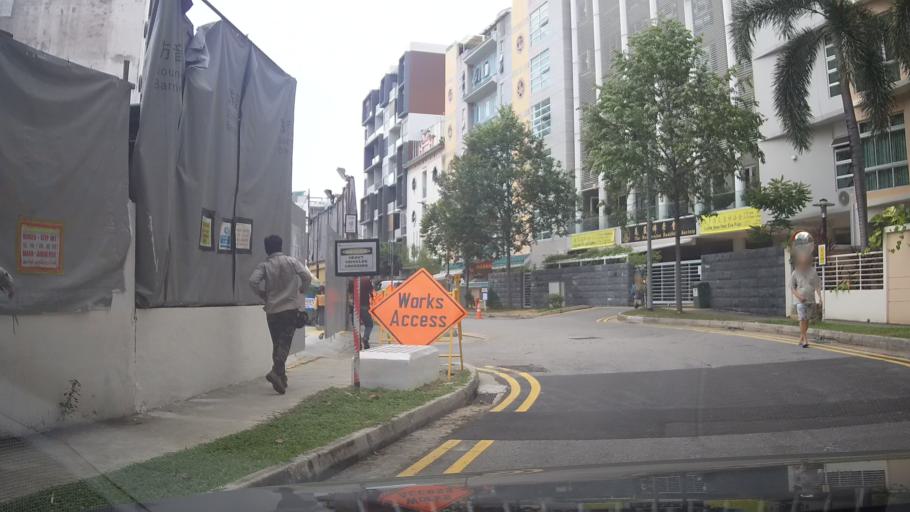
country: SG
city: Singapore
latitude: 1.3157
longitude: 103.8886
